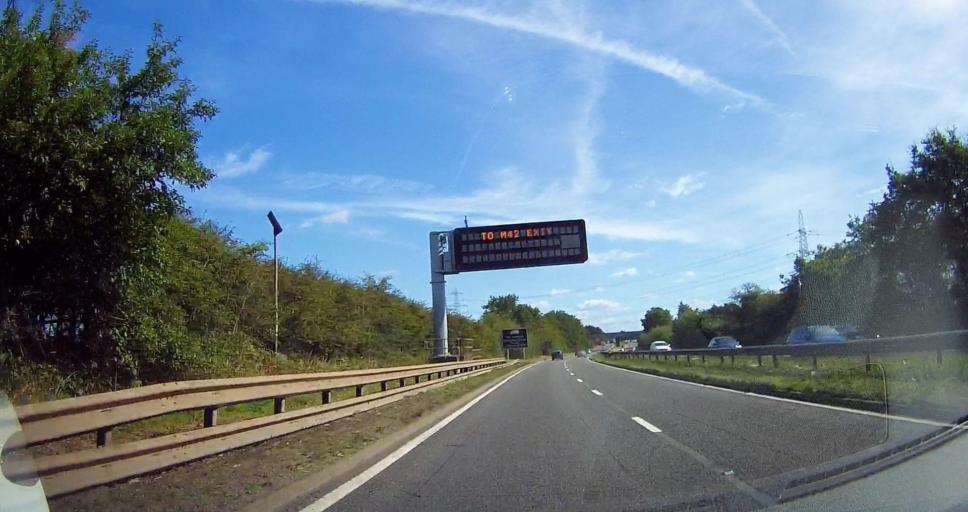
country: GB
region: England
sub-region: Staffordshire
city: Shenstone
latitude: 52.6530
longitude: -1.8450
